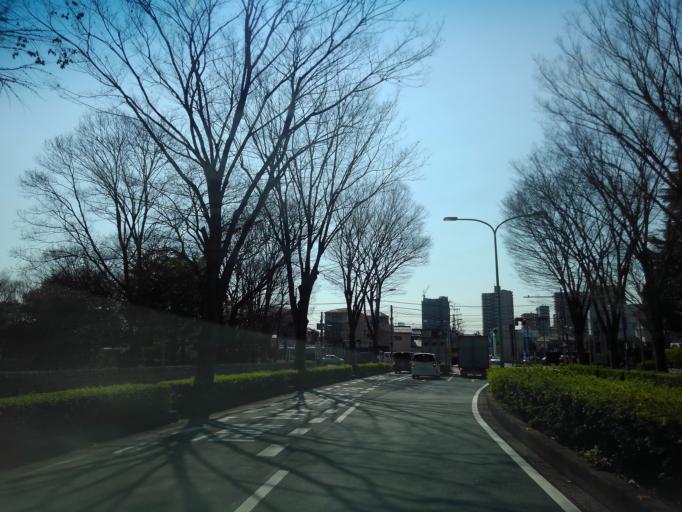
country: JP
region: Saitama
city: Tokorozawa
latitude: 35.7954
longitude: 139.4712
